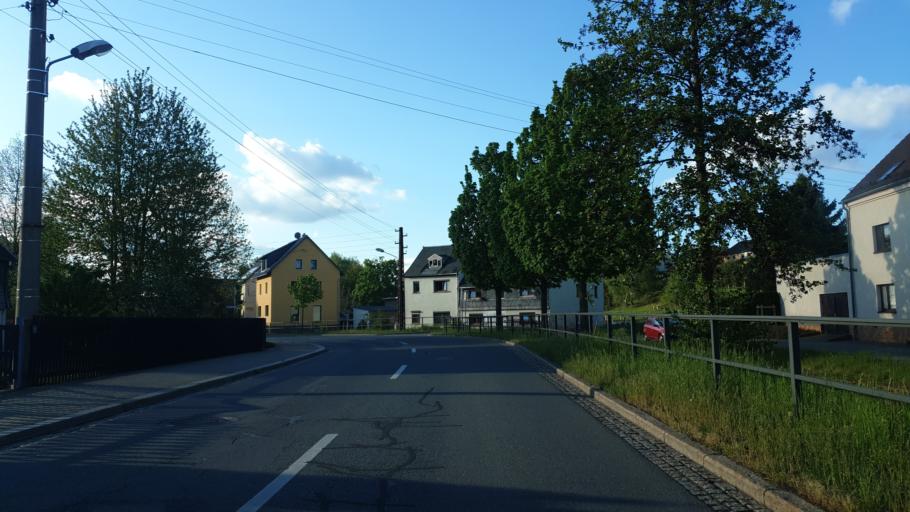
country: DE
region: Saxony
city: Oberlungwitz
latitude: 50.7654
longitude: 12.7077
